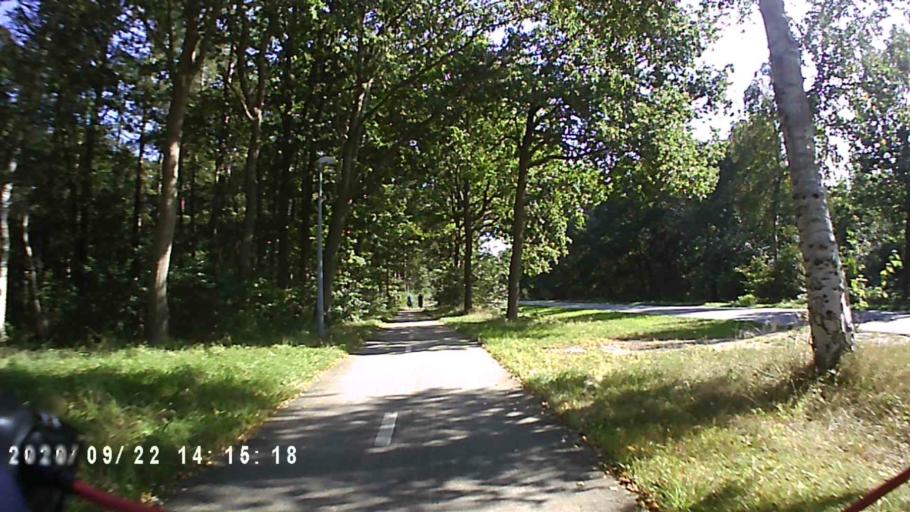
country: NL
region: Groningen
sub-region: Gemeente Leek
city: Leek
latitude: 53.0707
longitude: 6.4265
